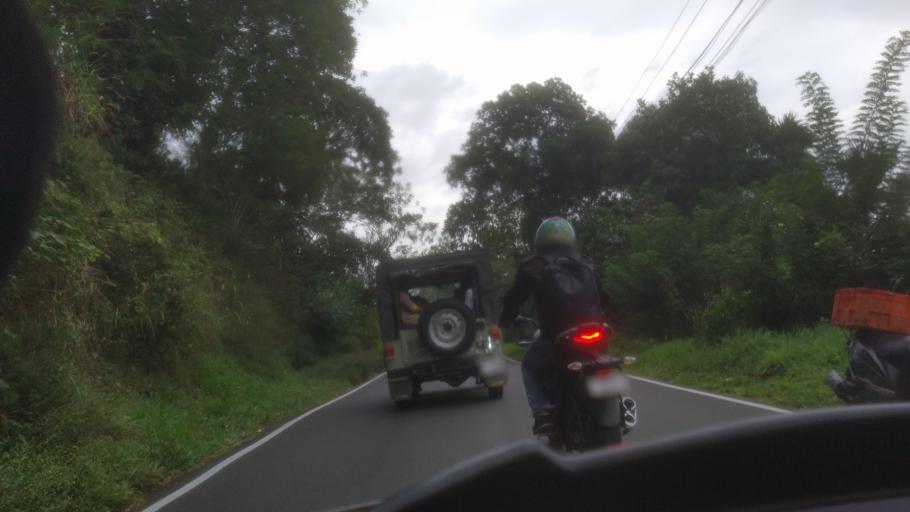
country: IN
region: Kerala
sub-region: Idukki
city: Idukki
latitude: 9.9413
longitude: 77.0241
